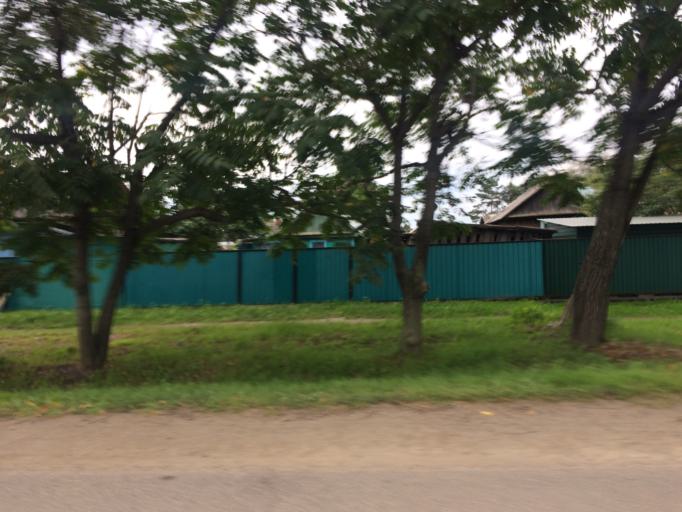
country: RU
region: Primorskiy
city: Dal'nerechensk
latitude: 45.9306
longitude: 133.7606
